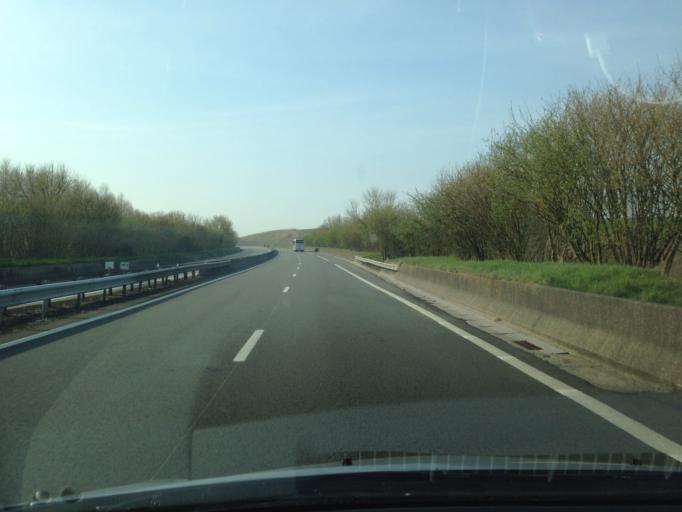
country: FR
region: Picardie
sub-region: Departement de la Somme
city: Rue
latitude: 50.3245
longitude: 1.7169
